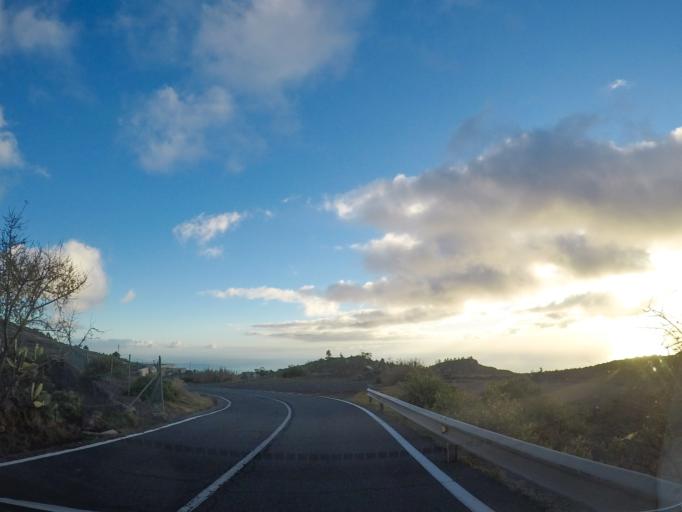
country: ES
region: Canary Islands
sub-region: Provincia de Santa Cruz de Tenerife
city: Alajero
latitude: 28.0731
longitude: -17.2382
